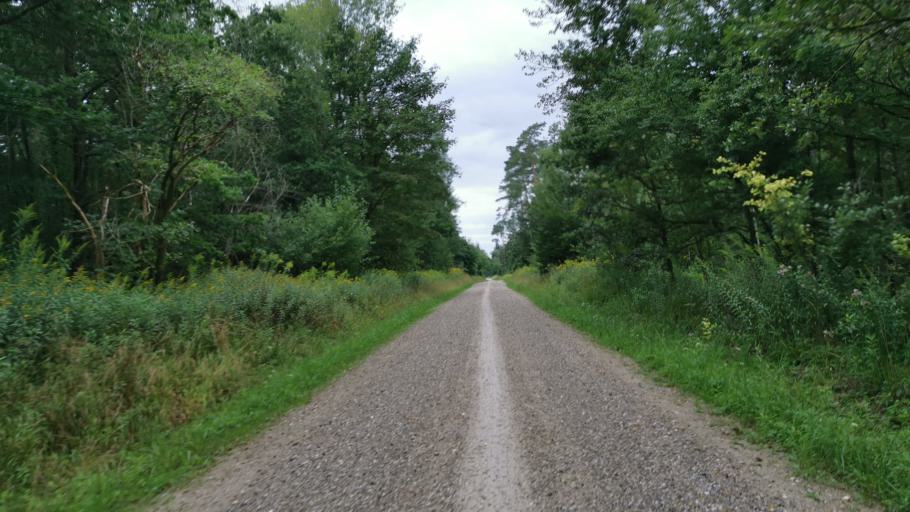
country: DE
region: Bavaria
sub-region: Upper Bavaria
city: Pullach im Isartal
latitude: 48.0692
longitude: 11.5661
